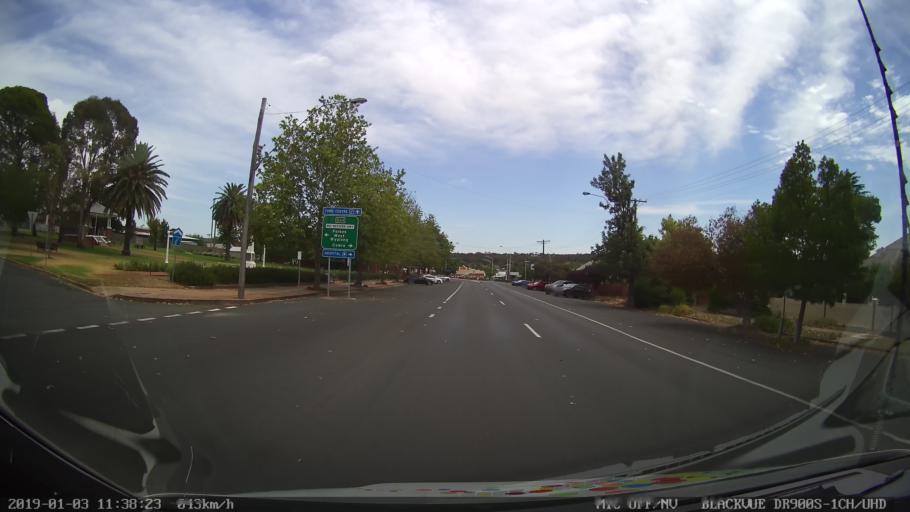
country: AU
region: New South Wales
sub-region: Weddin
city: Grenfell
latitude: -33.8966
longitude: 148.1624
